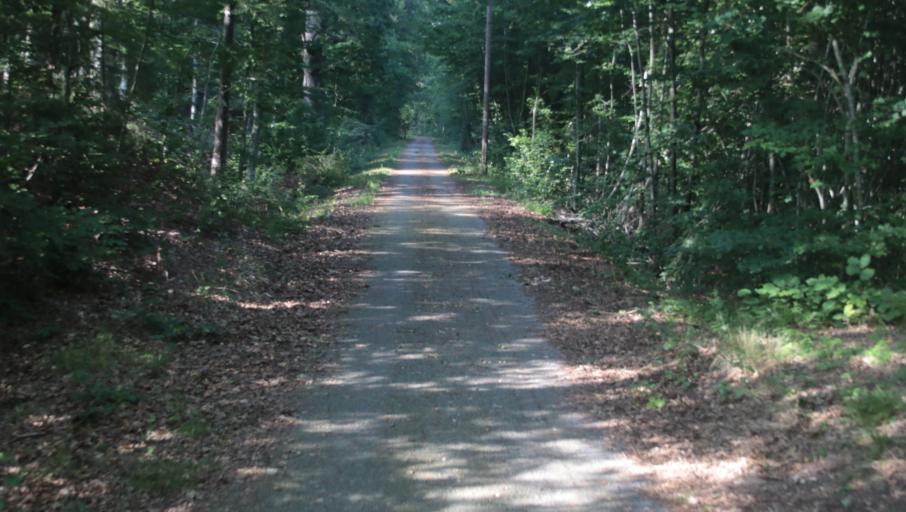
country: SE
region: Blekinge
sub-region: Karlshamns Kommun
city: Svangsta
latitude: 56.3826
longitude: 14.6779
